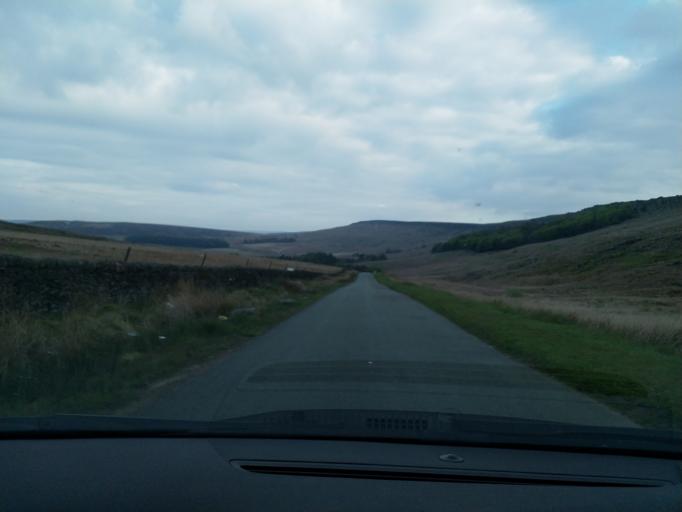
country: GB
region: England
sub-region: Derbyshire
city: Hathersage
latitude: 53.3441
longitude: -1.6356
